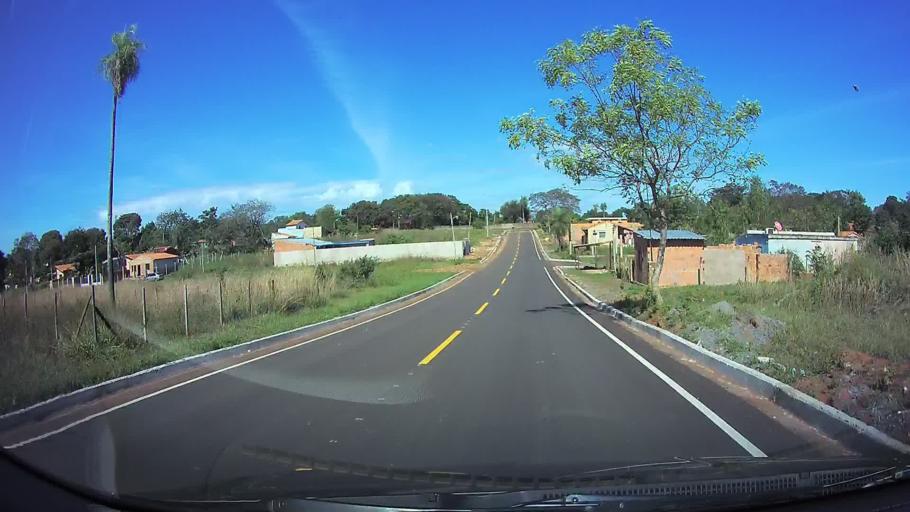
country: PY
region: Central
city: San Lorenzo
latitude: -25.2583
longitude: -57.4649
